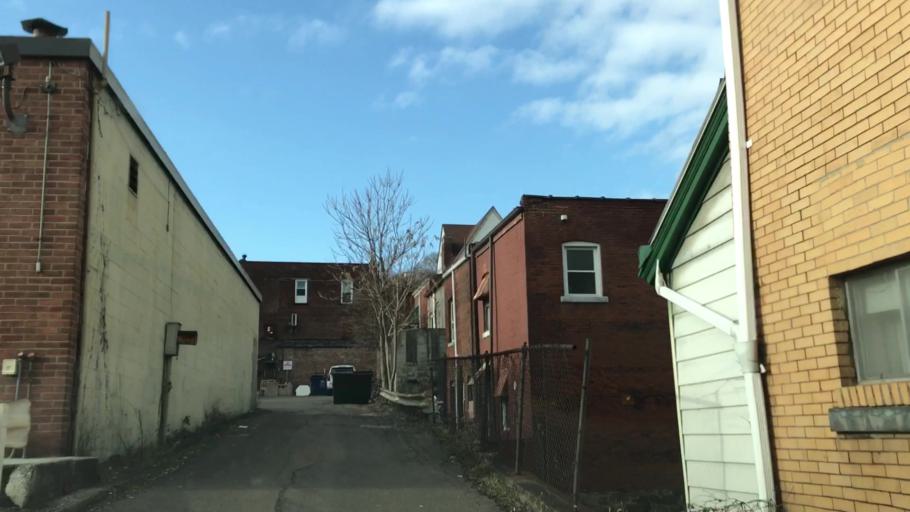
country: US
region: Pennsylvania
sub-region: Allegheny County
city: Bloomfield
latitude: 40.4525
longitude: -79.9513
